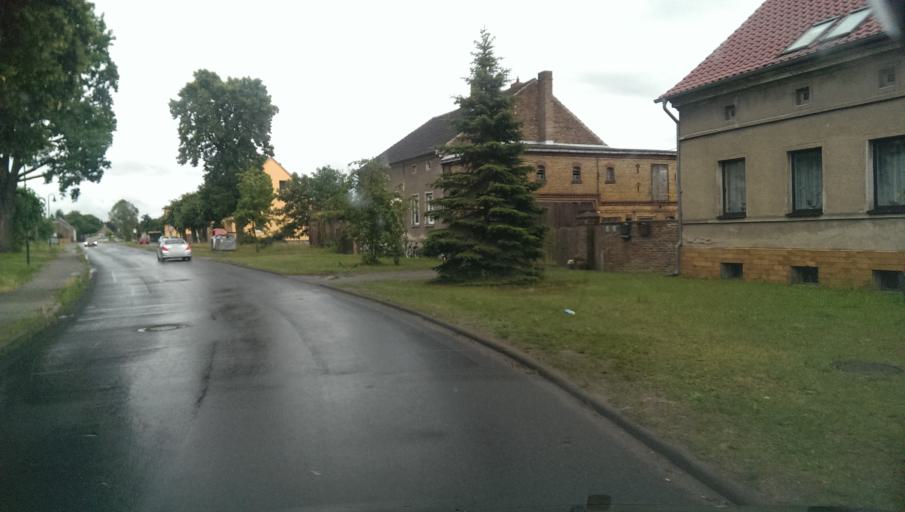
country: DE
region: Brandenburg
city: Gross Kreutz
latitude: 52.3621
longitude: 12.7443
